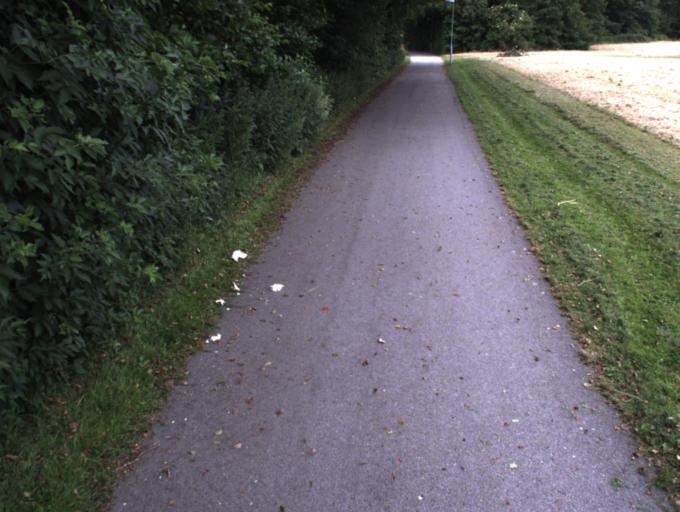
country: SE
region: Skane
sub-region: Helsingborg
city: Rydeback
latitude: 55.9655
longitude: 12.7637
